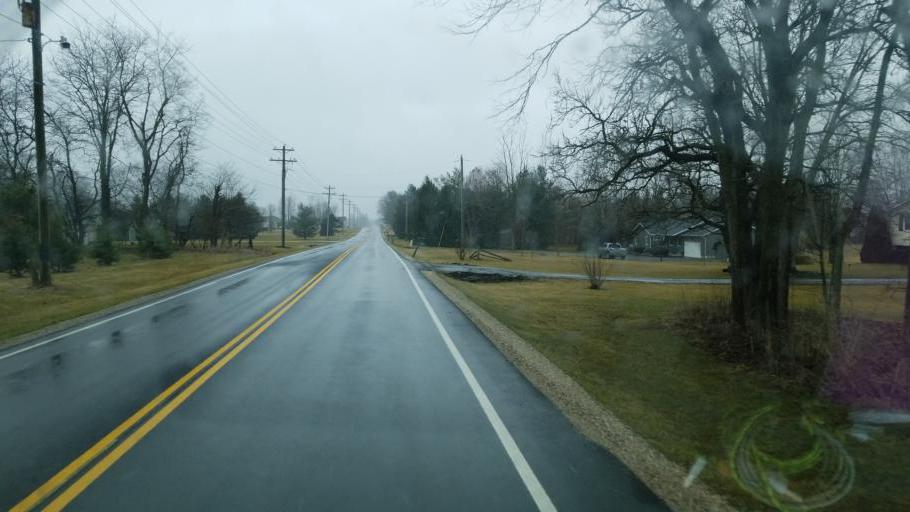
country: US
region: Ohio
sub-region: Union County
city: New California
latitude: 40.2134
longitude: -83.2696
